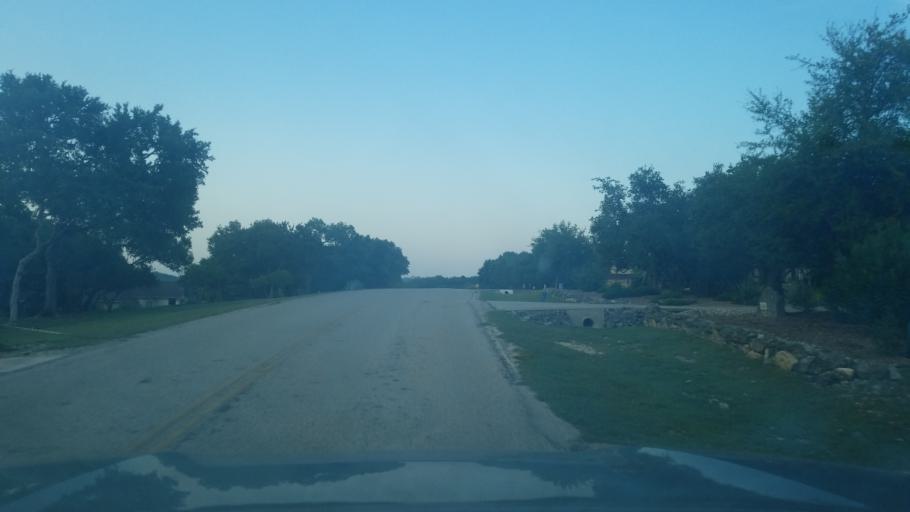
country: US
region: Texas
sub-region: Comal County
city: Bulverde
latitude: 29.8270
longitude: -98.4027
